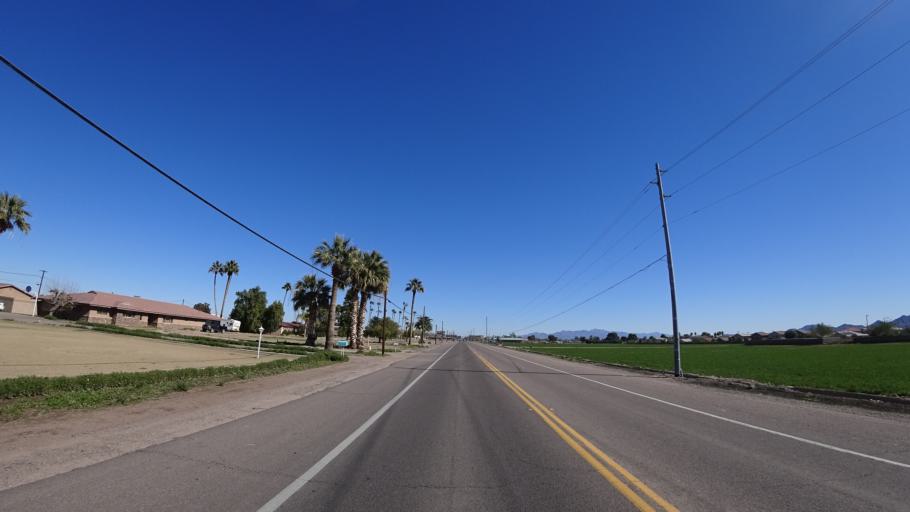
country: US
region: Arizona
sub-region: Maricopa County
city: Buckeye
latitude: 33.3705
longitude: -112.5965
